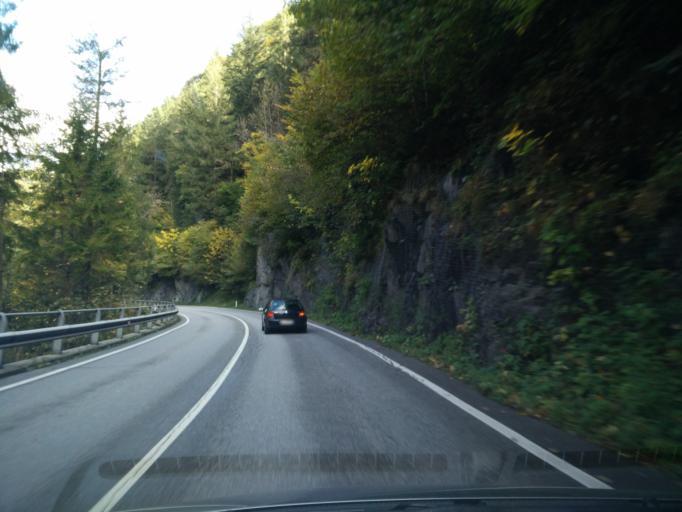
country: IT
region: Veneto
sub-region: Provincia di Belluno
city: Vigo di Cadore
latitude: 46.5250
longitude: 12.4674
